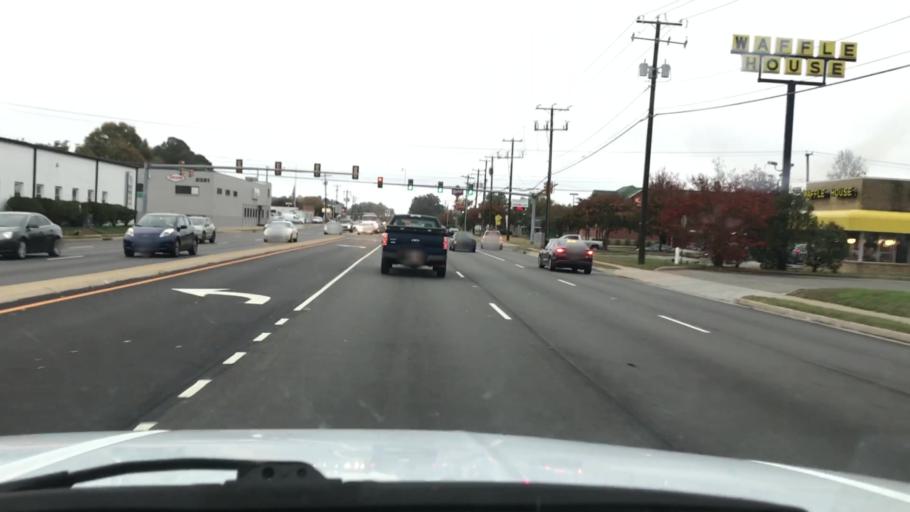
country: US
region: Virginia
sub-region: Henrico County
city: Chamberlayne
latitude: 37.6388
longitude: -77.4597
